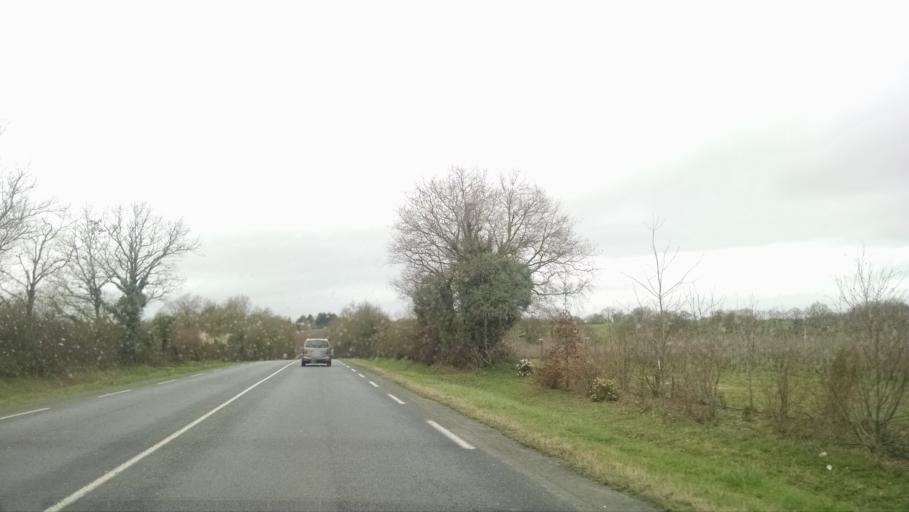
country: FR
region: Pays de la Loire
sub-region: Departement de la Loire-Atlantique
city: Remouille
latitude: 47.0624
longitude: -1.3832
